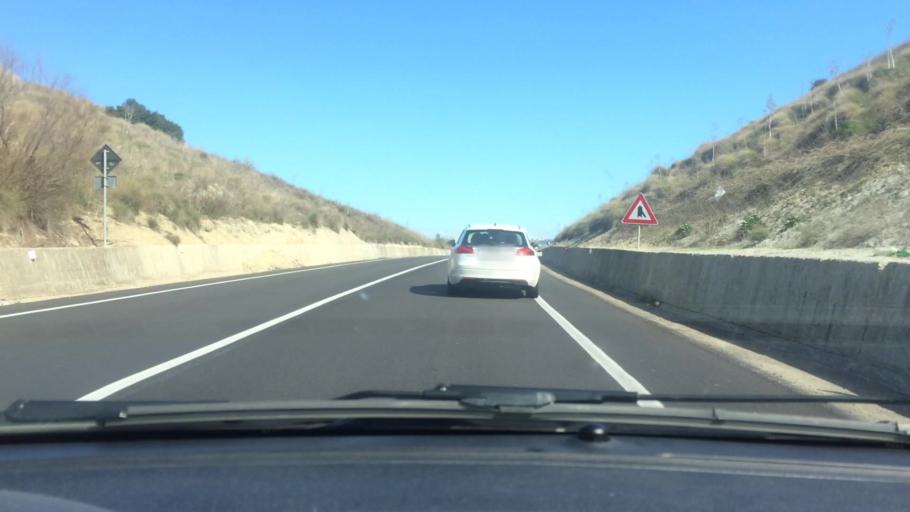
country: IT
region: Basilicate
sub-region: Provincia di Matera
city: La Martella
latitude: 40.6015
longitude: 16.5663
